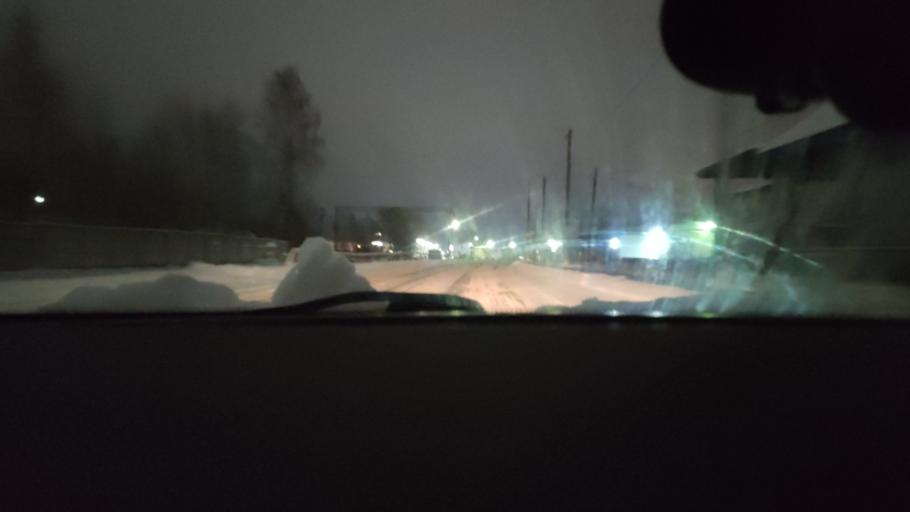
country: RU
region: Perm
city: Krasnokamsk
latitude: 58.0732
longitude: 55.7746
